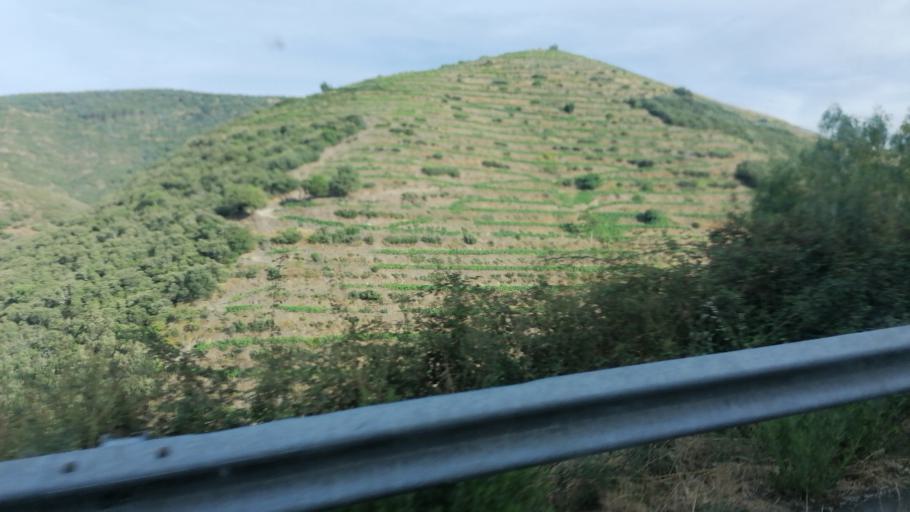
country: PT
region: Viseu
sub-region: Sao Joao da Pesqueira
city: Sao Joao da Pesqueira
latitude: 41.1194
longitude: -7.4525
